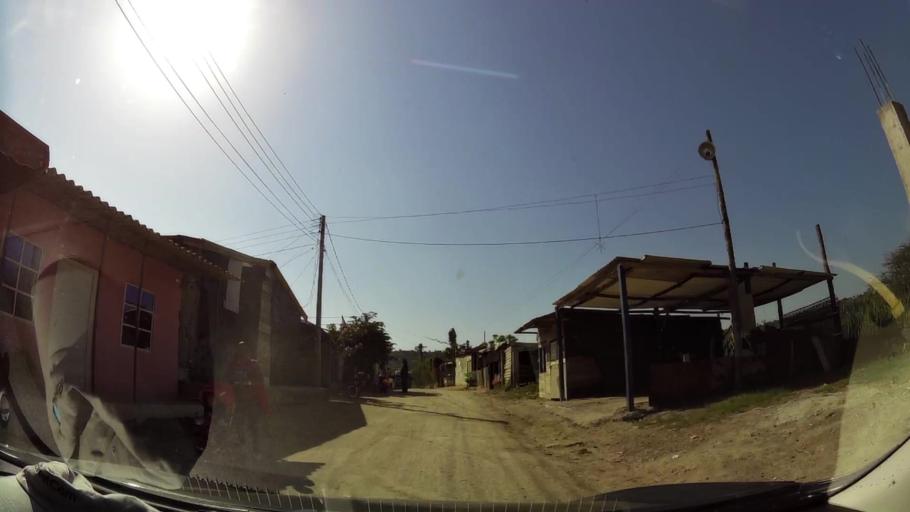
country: CO
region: Bolivar
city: Cartagena
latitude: 10.3686
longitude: -75.4992
